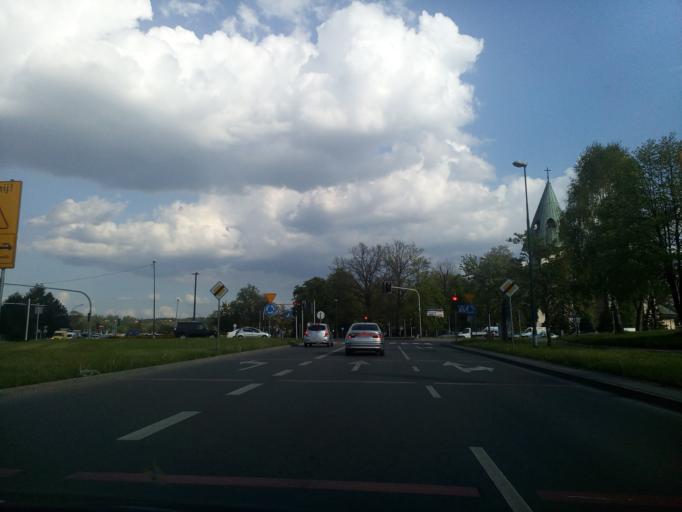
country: PL
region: Lesser Poland Voivodeship
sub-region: Powiat nowosadecki
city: Nowy Sacz
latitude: 49.6180
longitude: 20.7135
